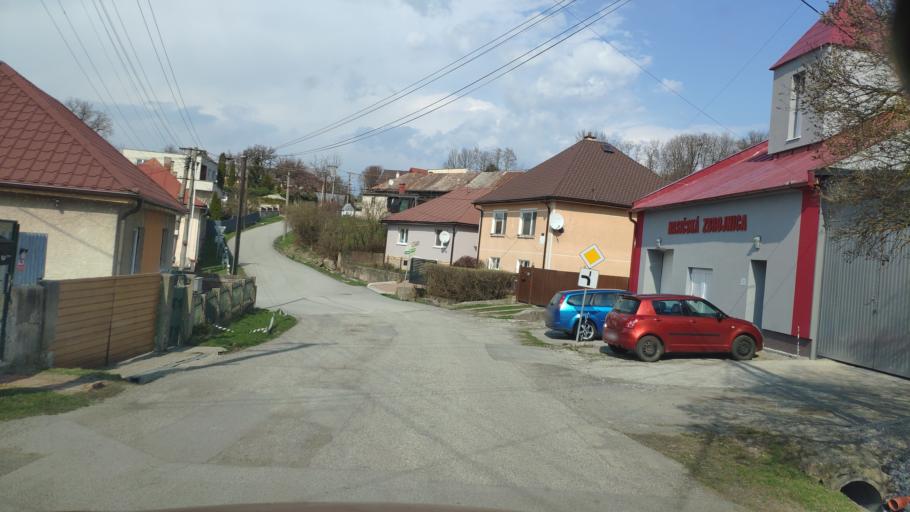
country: SK
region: Kosicky
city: Kosice
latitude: 48.6249
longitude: 21.3672
